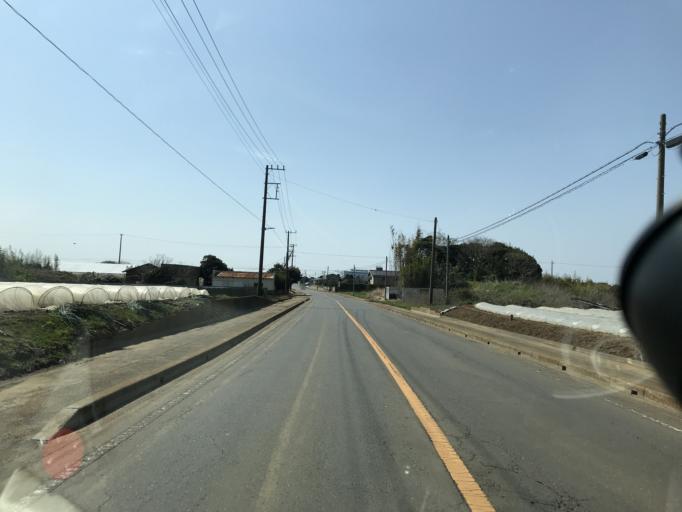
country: JP
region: Chiba
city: Asahi
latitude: 35.7909
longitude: 140.6971
